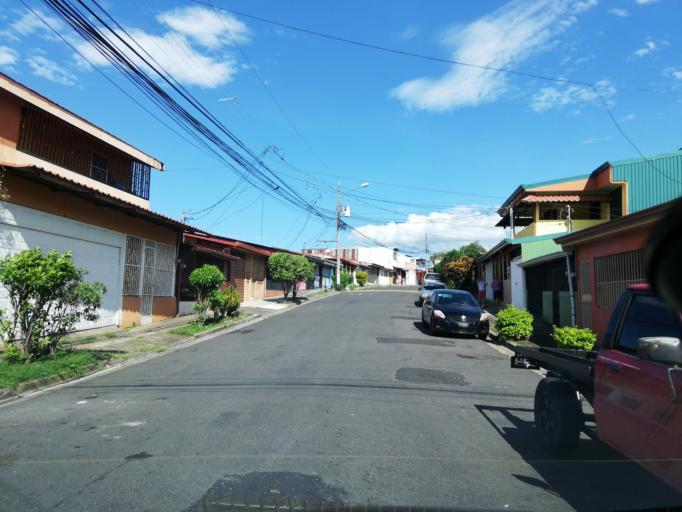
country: CR
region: Alajuela
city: Alajuela
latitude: 10.0036
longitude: -84.2049
